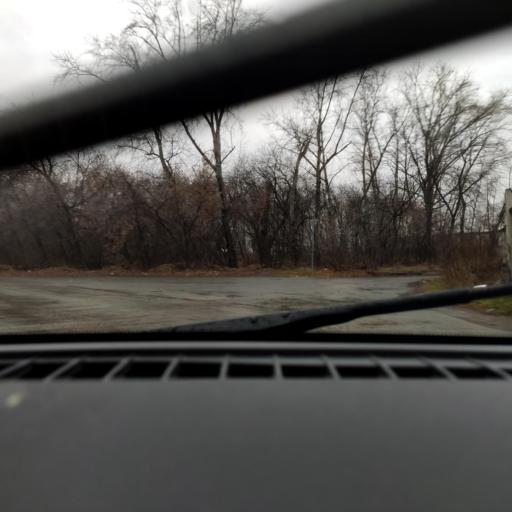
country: RU
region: Perm
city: Kultayevo
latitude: 58.0000
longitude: 55.9379
